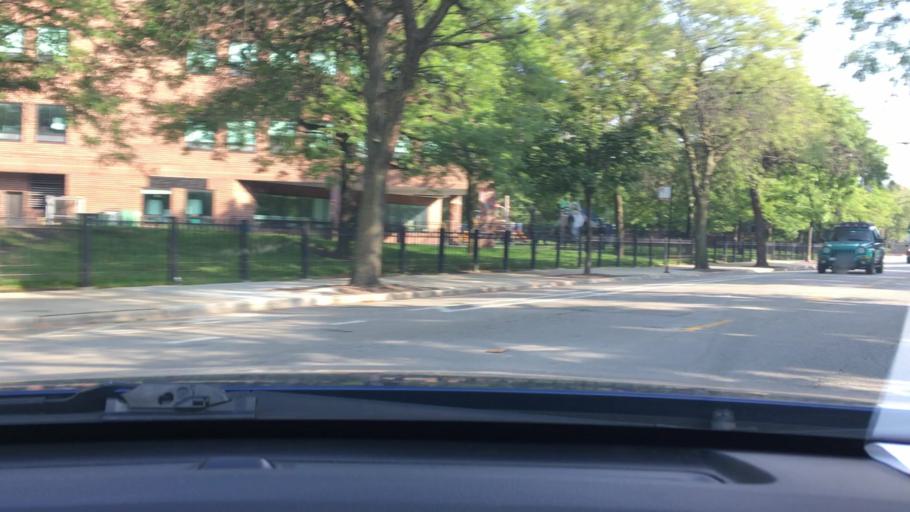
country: US
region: Illinois
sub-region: Cook County
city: Chicago
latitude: 41.8751
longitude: -87.6619
